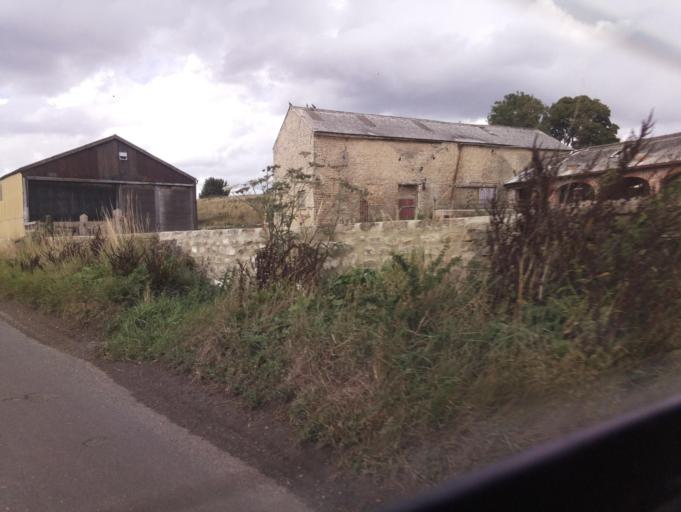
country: GB
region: England
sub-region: North Yorkshire
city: Bedale
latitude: 54.2142
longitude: -1.6283
